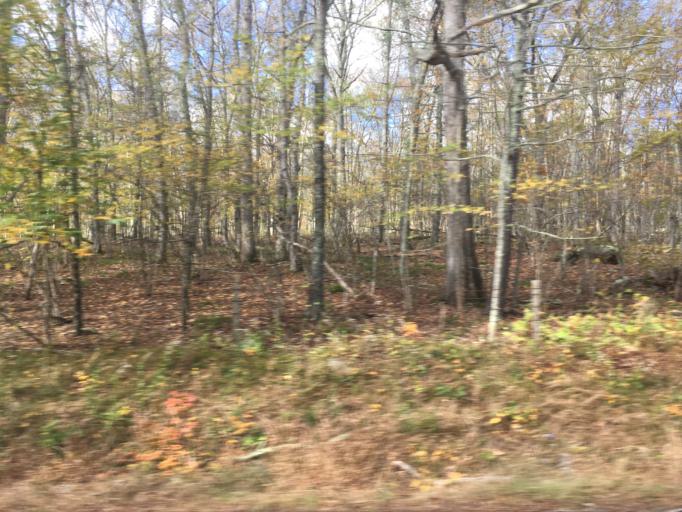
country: US
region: Rhode Island
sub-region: Providence County
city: North Scituate
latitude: 41.7975
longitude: -71.6581
